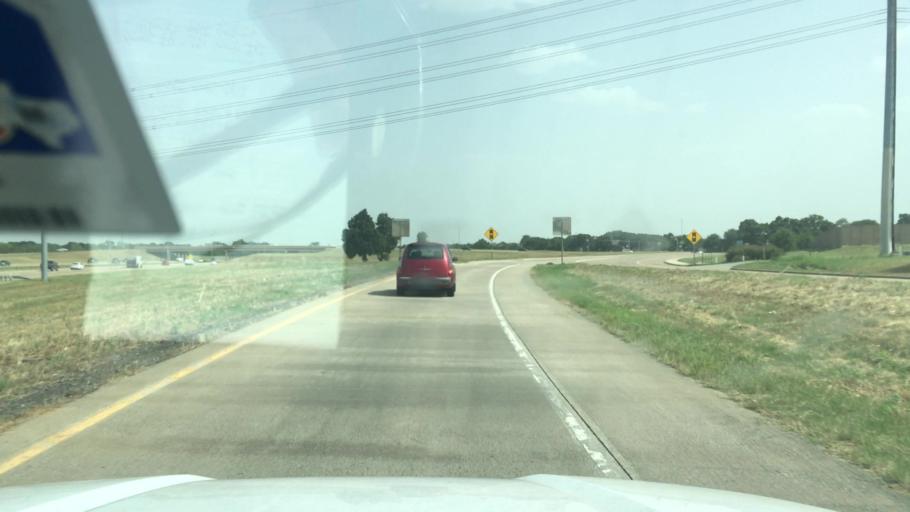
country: US
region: Texas
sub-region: Tarrant County
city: Euless
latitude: 32.8710
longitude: -97.0683
